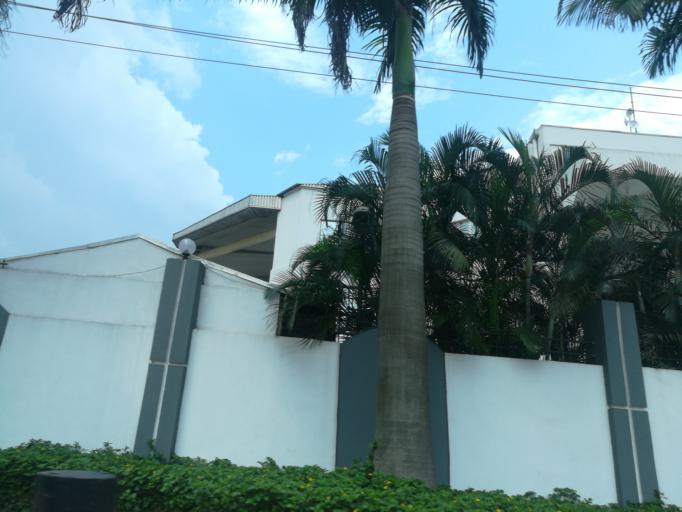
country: NG
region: Lagos
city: Ikeja
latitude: 6.6062
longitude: 3.3650
